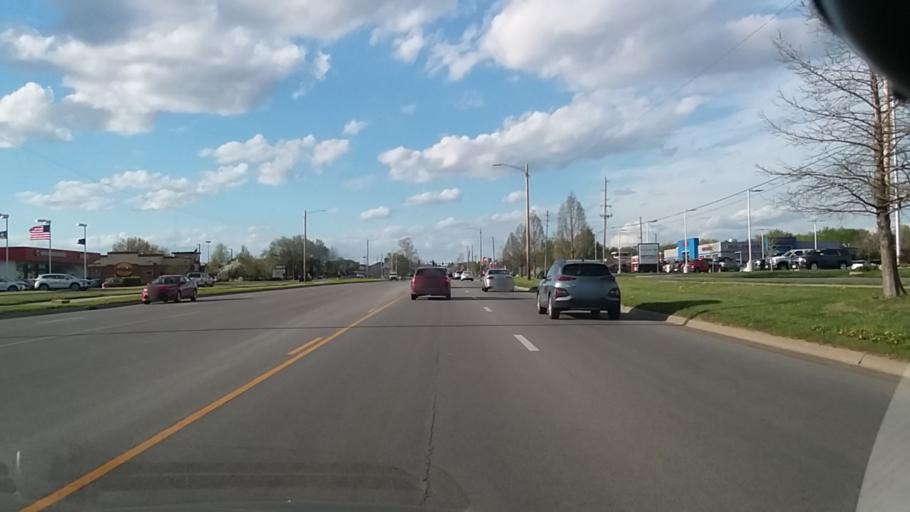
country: US
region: Kansas
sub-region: Douglas County
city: Lawrence
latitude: 38.9315
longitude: -95.2605
